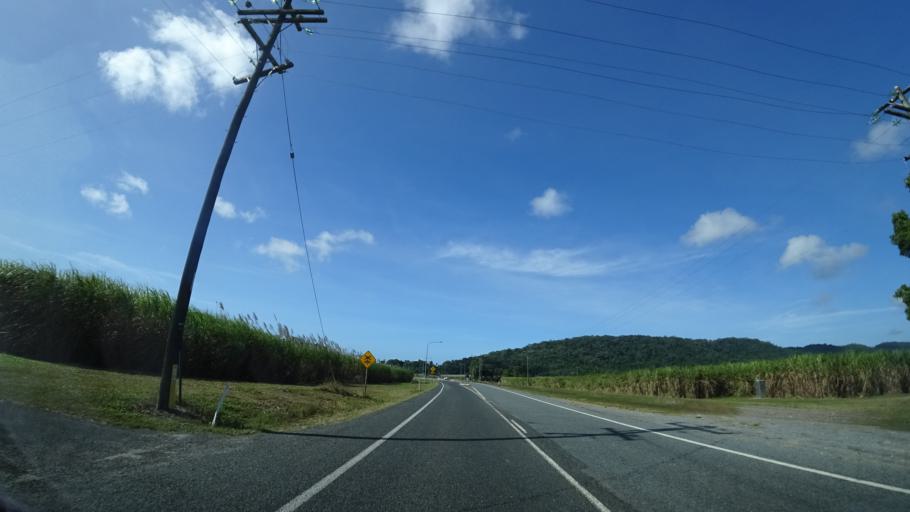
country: AU
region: Queensland
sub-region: Cairns
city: Port Douglas
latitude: -16.4832
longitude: 145.3883
